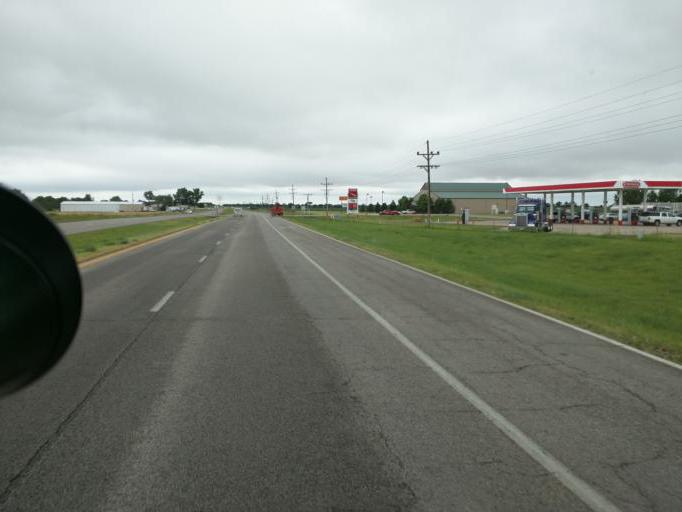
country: US
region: Kansas
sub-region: Reno County
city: South Hutchinson
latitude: 38.0091
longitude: -97.9403
